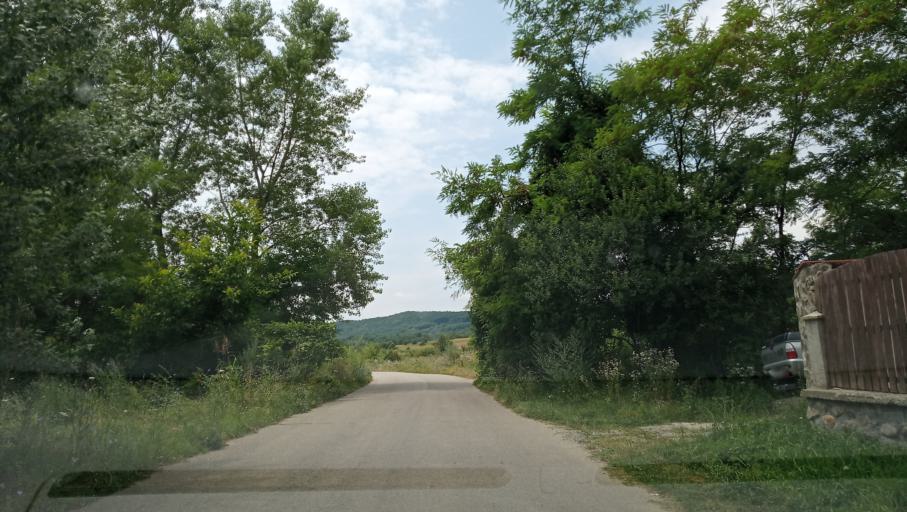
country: RO
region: Gorj
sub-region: Comuna Bumbesti-Jiu
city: Bumbesti-Jiu
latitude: 45.1730
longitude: 23.3595
